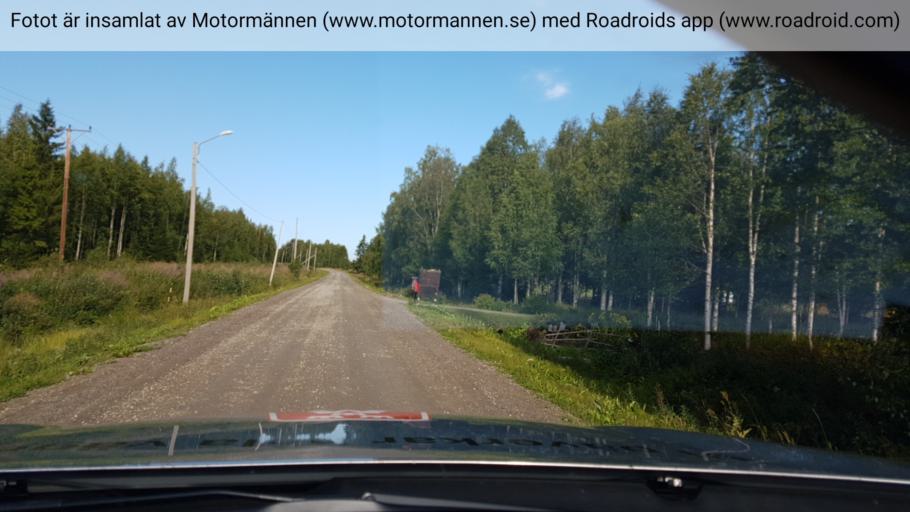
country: SE
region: Norrbotten
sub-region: Kalix Kommun
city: Kalix
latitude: 66.1137
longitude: 23.2807
